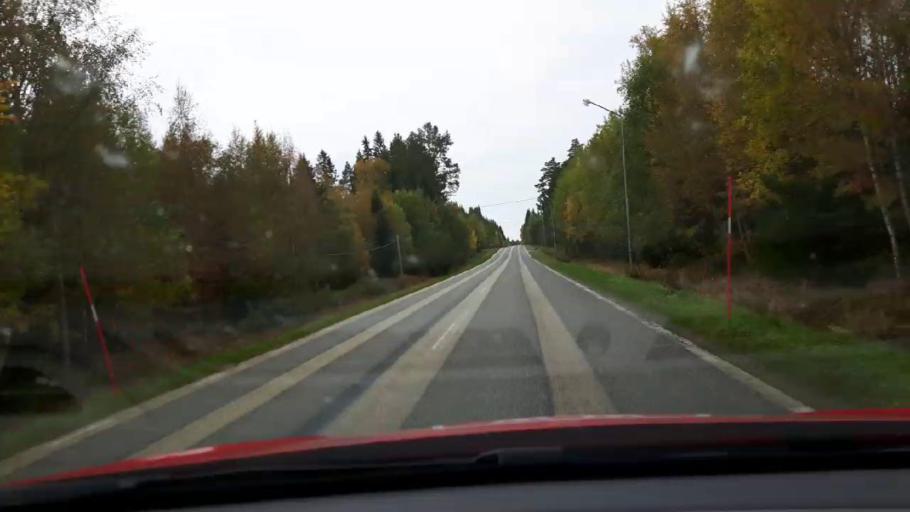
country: SE
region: Jaemtland
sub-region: Bergs Kommun
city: Hoverberg
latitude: 62.8954
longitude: 14.3481
